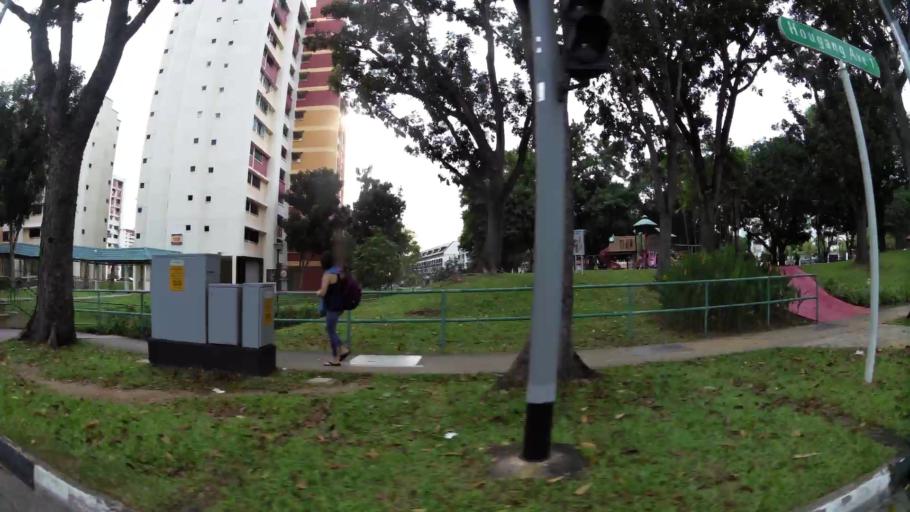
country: SG
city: Singapore
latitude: 1.3556
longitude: 103.8899
